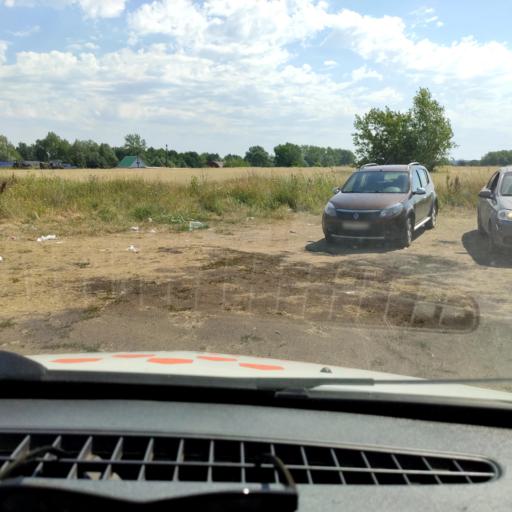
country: RU
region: Bashkortostan
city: Ufa
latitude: 54.8202
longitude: 55.9976
